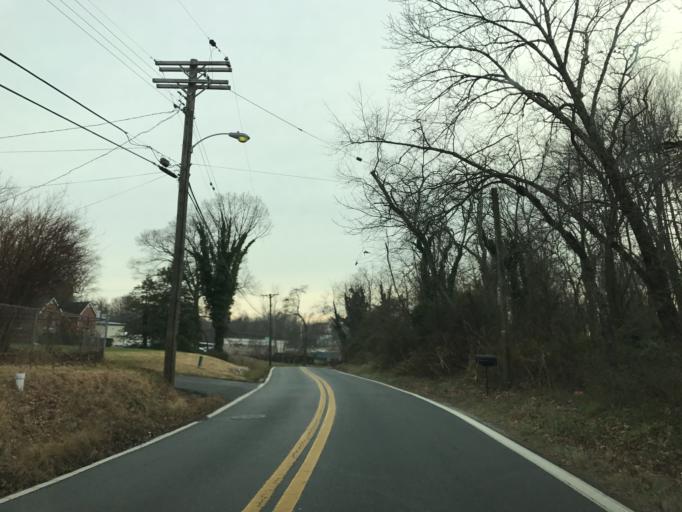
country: US
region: Maryland
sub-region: Baltimore County
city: White Marsh
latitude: 39.3914
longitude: -76.4161
